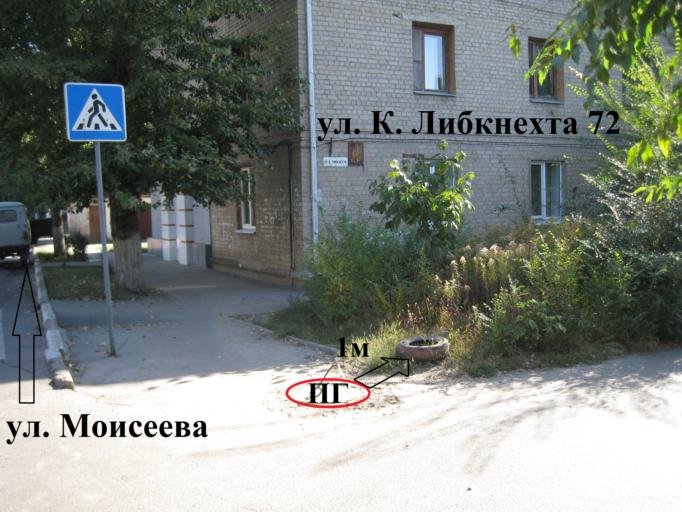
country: RU
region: Voronezj
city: Voronezh
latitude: 51.6484
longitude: 39.1719
